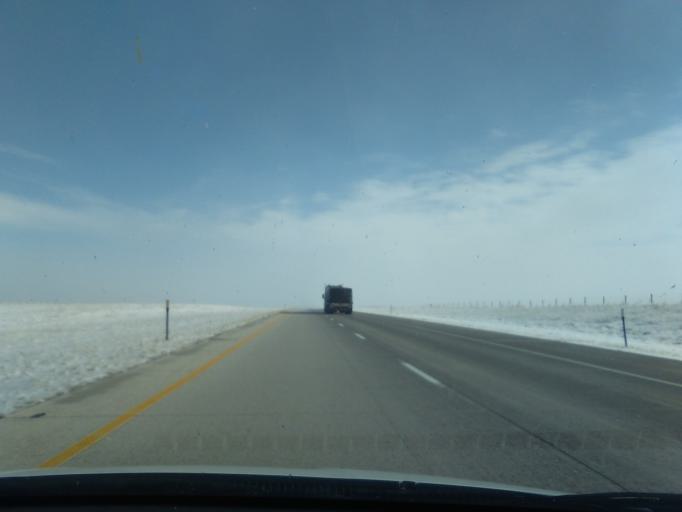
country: US
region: Wyoming
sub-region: Laramie County
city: Pine Bluffs
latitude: 41.1575
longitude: -104.3972
